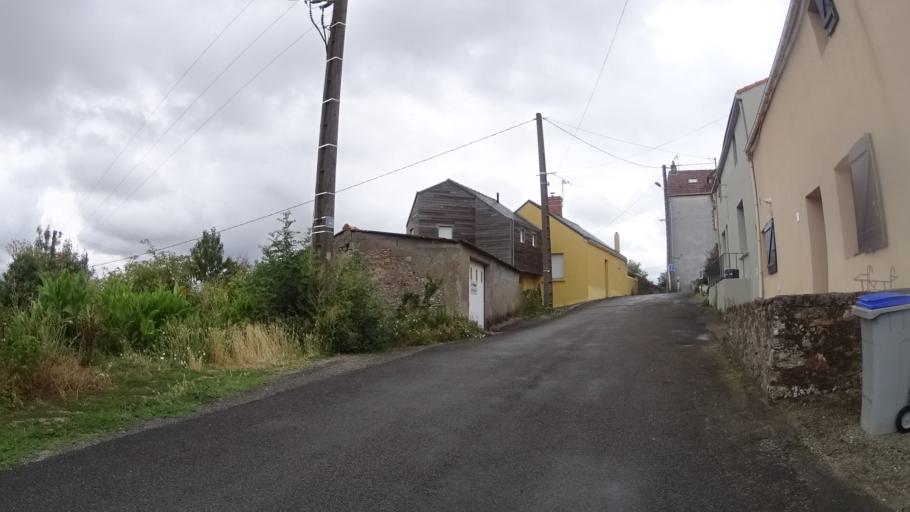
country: FR
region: Pays de la Loire
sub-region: Departement de la Loire-Atlantique
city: Le Pellerin
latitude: 47.2059
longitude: -1.7781
